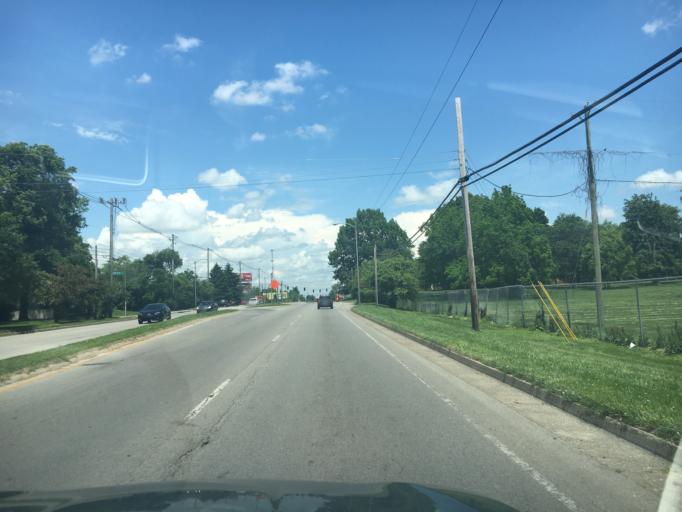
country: US
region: Kentucky
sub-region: Fayette County
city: Mount Vernon
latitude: 38.0653
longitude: -84.4990
